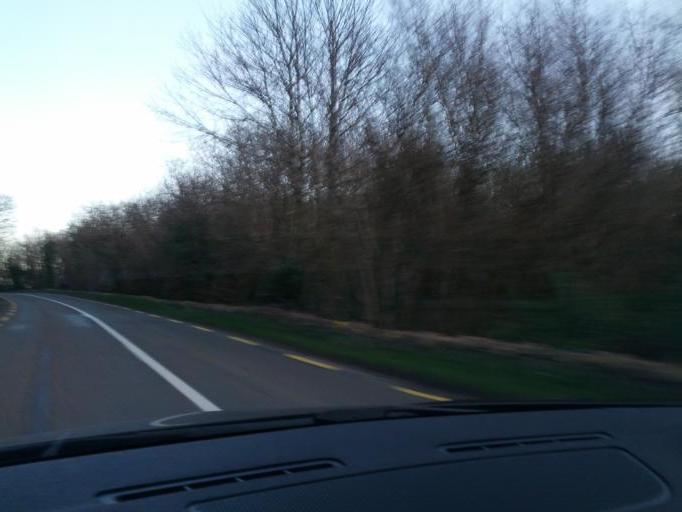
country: IE
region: Connaught
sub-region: Sligo
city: Ballymote
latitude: 53.9738
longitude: -8.4480
